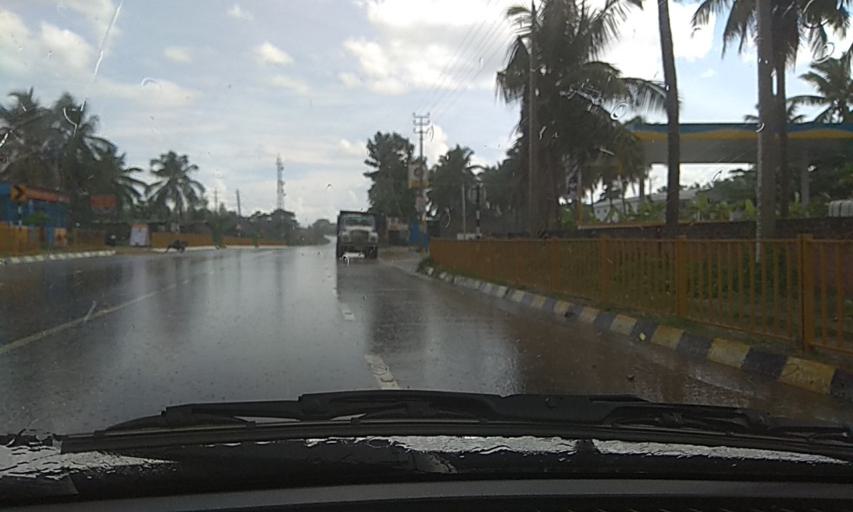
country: IN
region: Karnataka
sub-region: Mandya
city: Maddur
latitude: 12.6882
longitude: 77.0591
